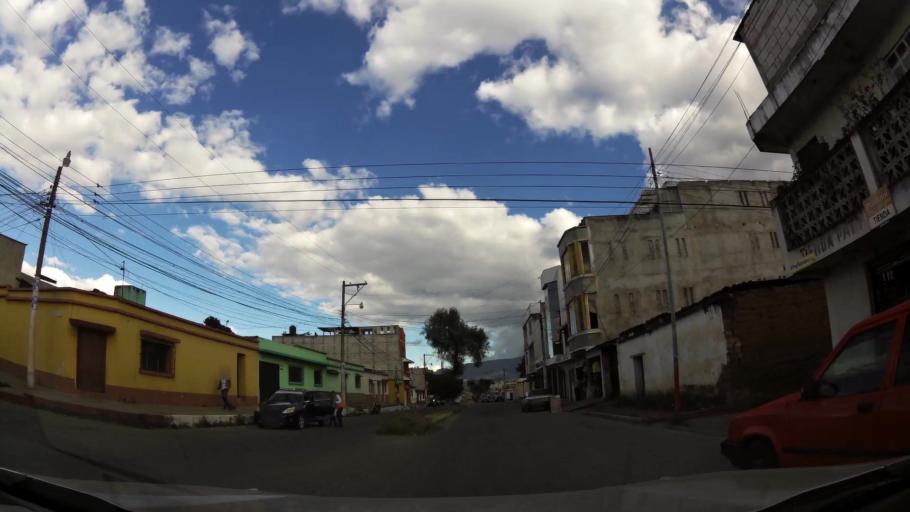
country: GT
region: Quetzaltenango
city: Quetzaltenango
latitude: 14.8475
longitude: -91.5178
